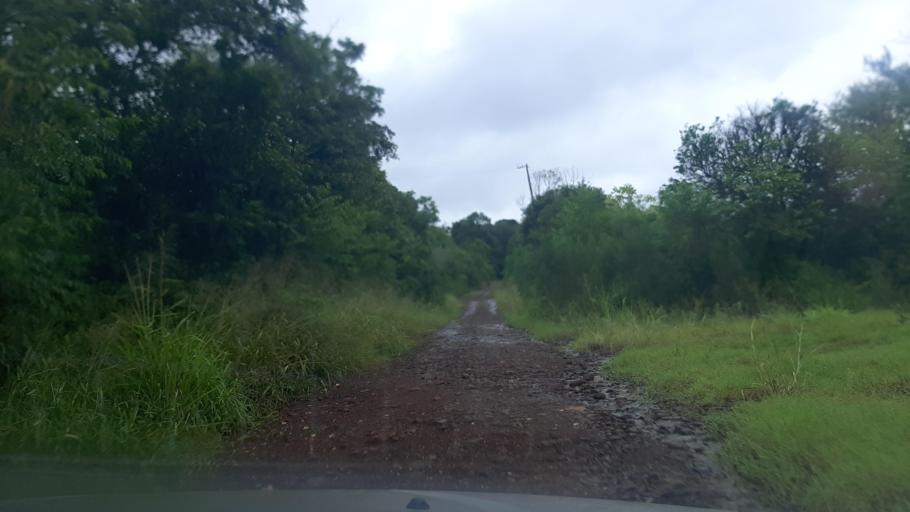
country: BR
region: Parana
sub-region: Ampere
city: Ampere
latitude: -26.0483
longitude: -53.5202
